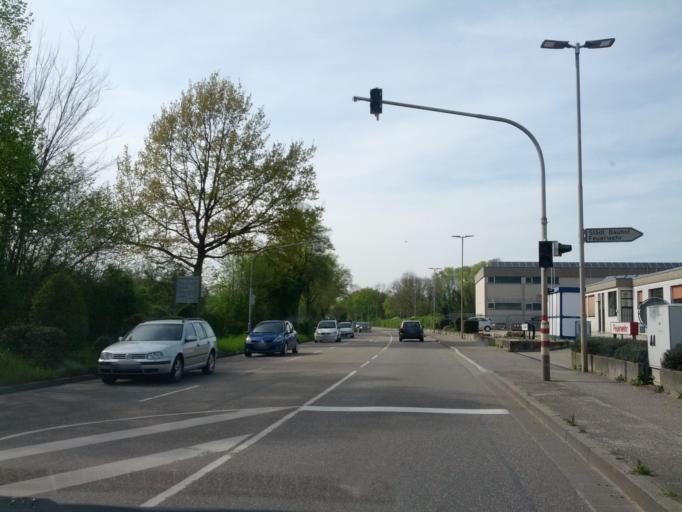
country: DE
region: Baden-Wuerttemberg
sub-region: Freiburg Region
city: Emmendingen
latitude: 48.1189
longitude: 7.8457
